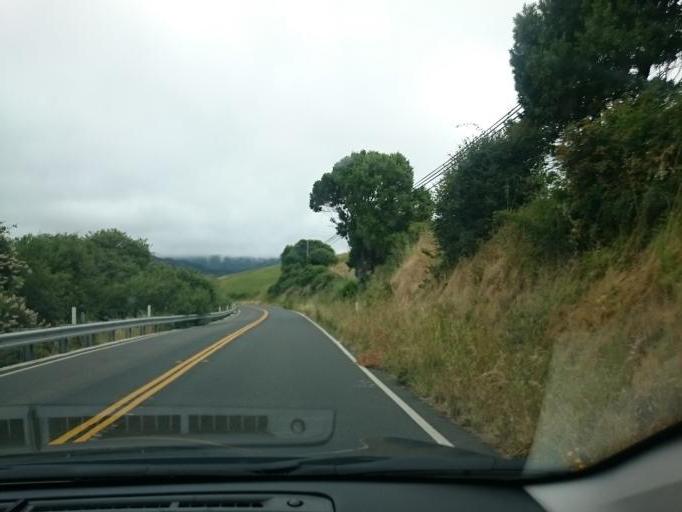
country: US
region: California
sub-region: Marin County
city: Inverness
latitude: 38.0916
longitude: -122.8194
